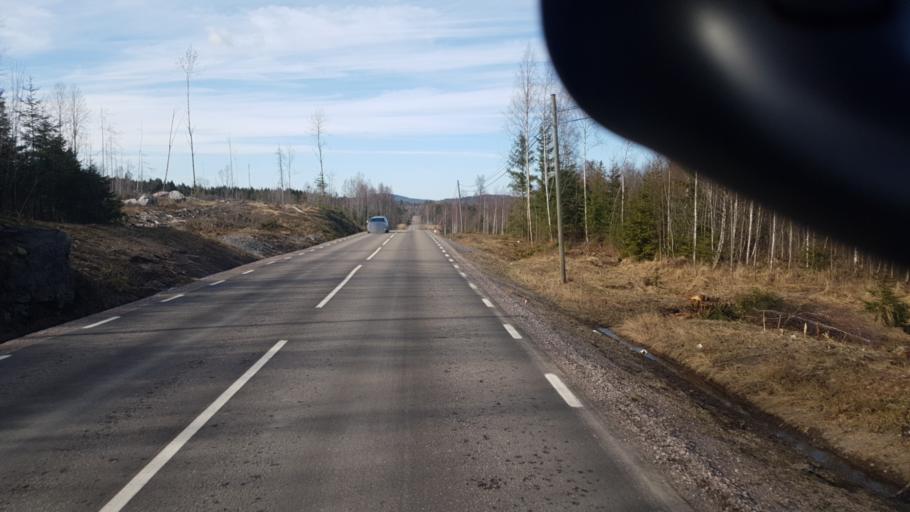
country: SE
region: Vaermland
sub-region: Eda Kommun
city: Amotfors
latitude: 59.7416
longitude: 12.3793
